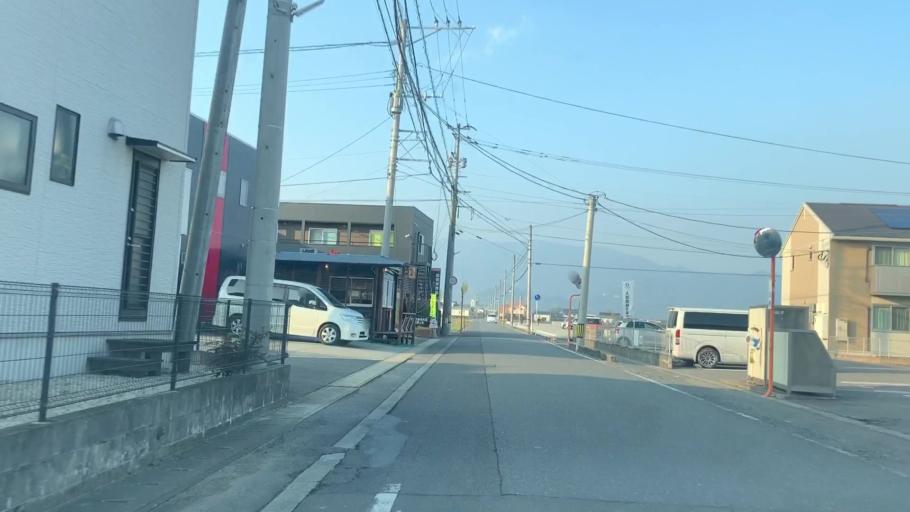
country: JP
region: Saga Prefecture
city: Saga-shi
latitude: 33.2729
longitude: 130.2284
